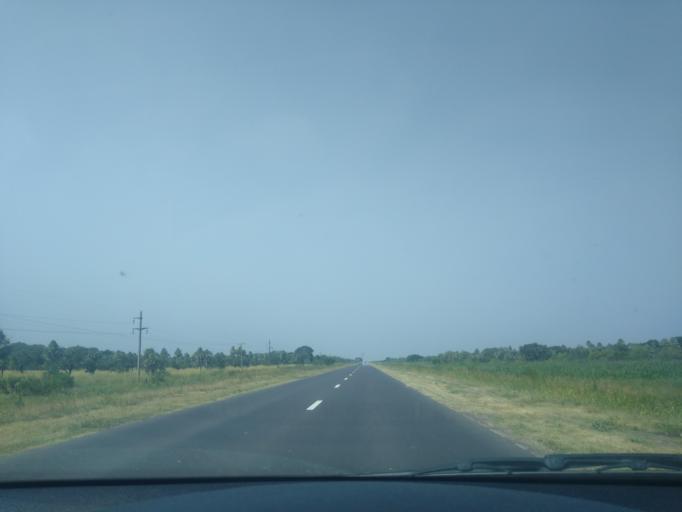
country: AR
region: Chaco
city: Fontana
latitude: -27.5531
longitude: -59.1431
